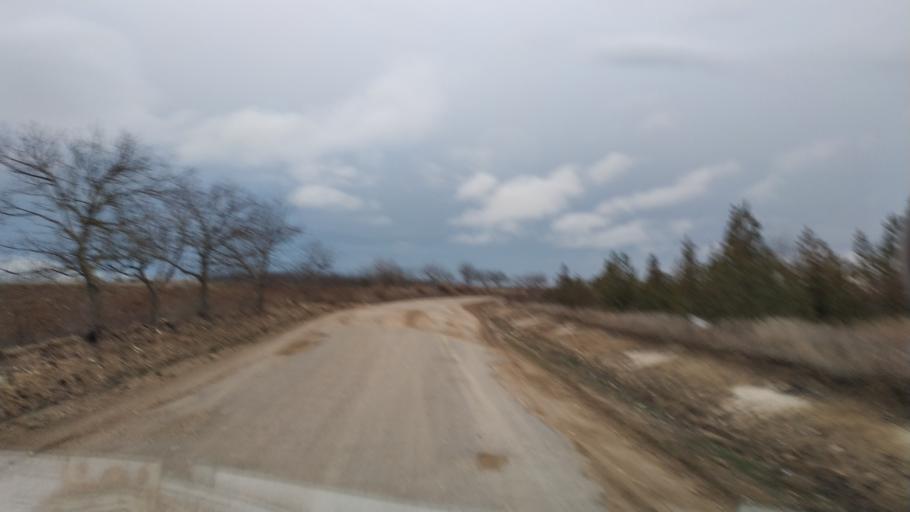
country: MD
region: Causeni
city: Causeni
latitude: 46.6139
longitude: 29.3991
